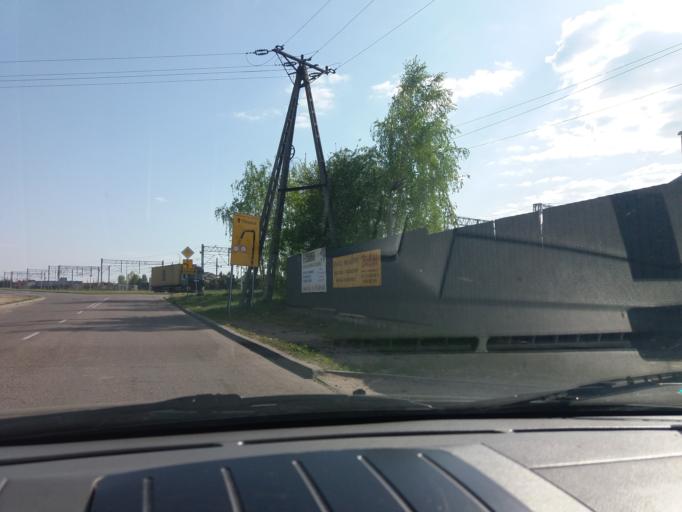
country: PL
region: Masovian Voivodeship
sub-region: Powiat mlawski
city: Mlawa
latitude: 53.1168
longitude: 20.3590
